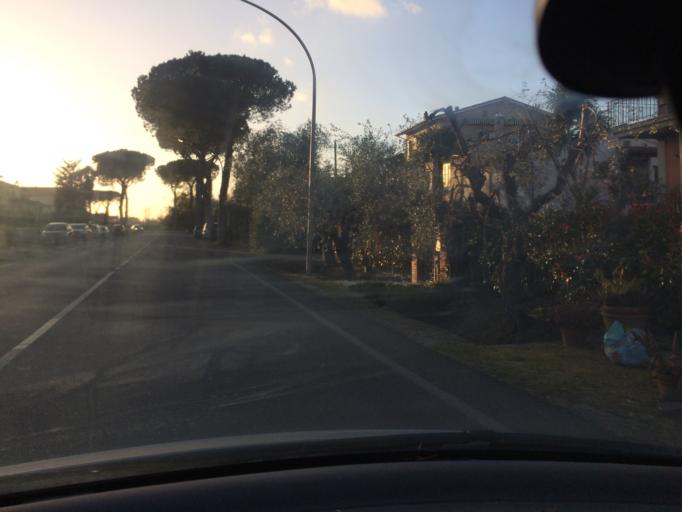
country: IT
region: Tuscany
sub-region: Province of Pisa
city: Gello
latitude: 43.7230
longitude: 10.4371
